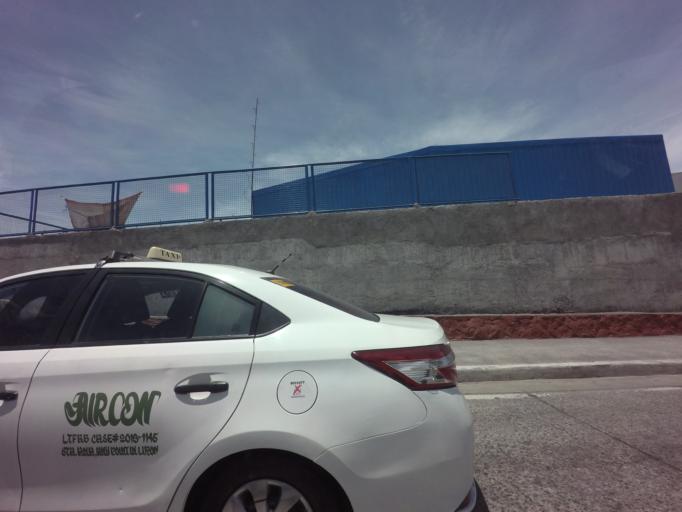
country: PH
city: Sambayanihan People's Village
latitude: 14.4955
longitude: 120.9994
